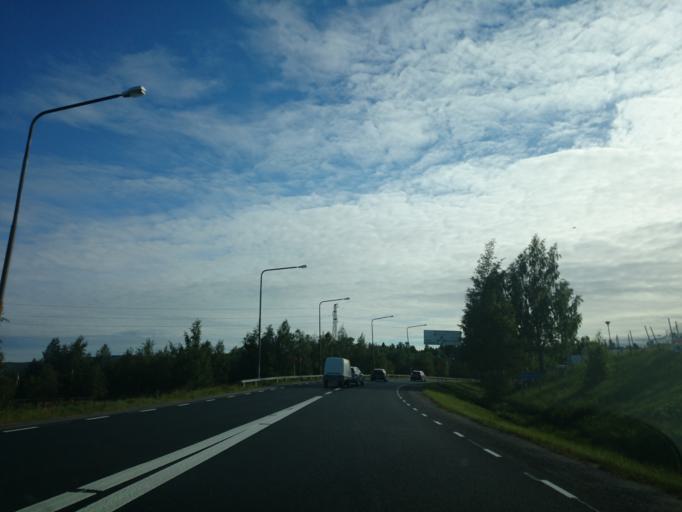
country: SE
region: Vaesternorrland
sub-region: Sundsvalls Kommun
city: Sundsvall
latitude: 62.4118
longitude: 17.3365
